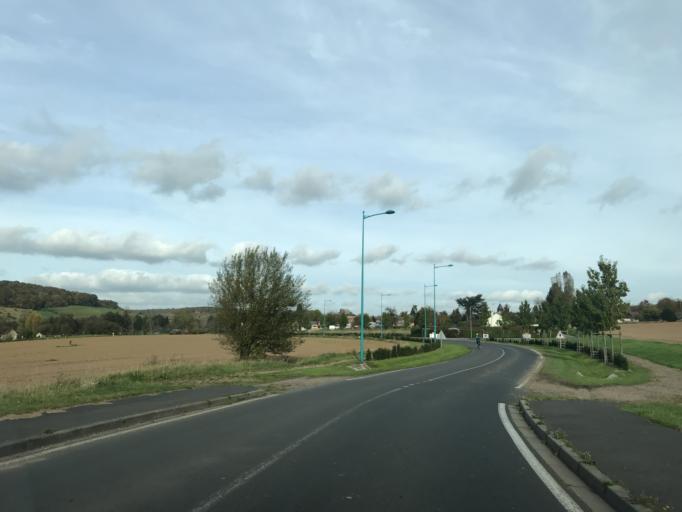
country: FR
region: Haute-Normandie
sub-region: Departement de l'Eure
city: Perriers-sur-Andelle
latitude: 49.4555
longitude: 1.3908
